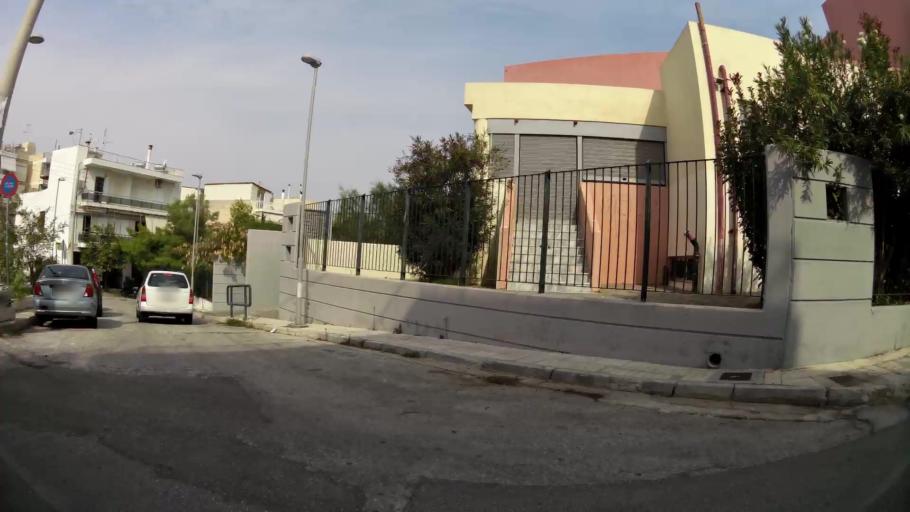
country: GR
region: Attica
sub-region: Nomarchia Athinas
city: Agios Dimitrios
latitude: 37.9315
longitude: 23.7379
